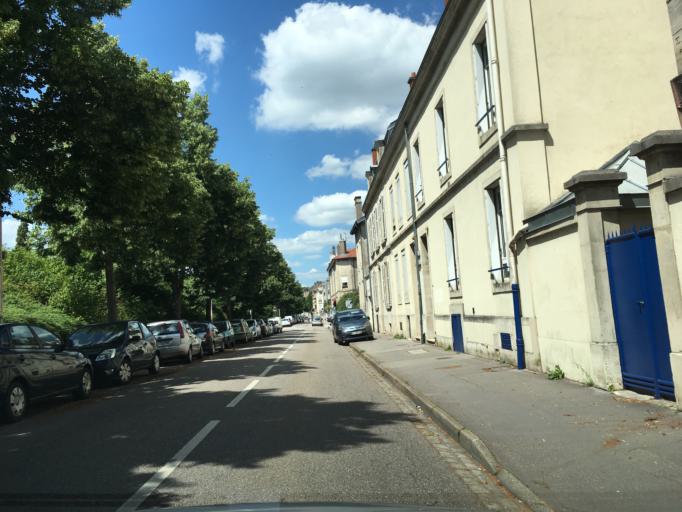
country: FR
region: Lorraine
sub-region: Departement de Meurthe-et-Moselle
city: Maxeville
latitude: 48.6986
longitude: 6.1700
